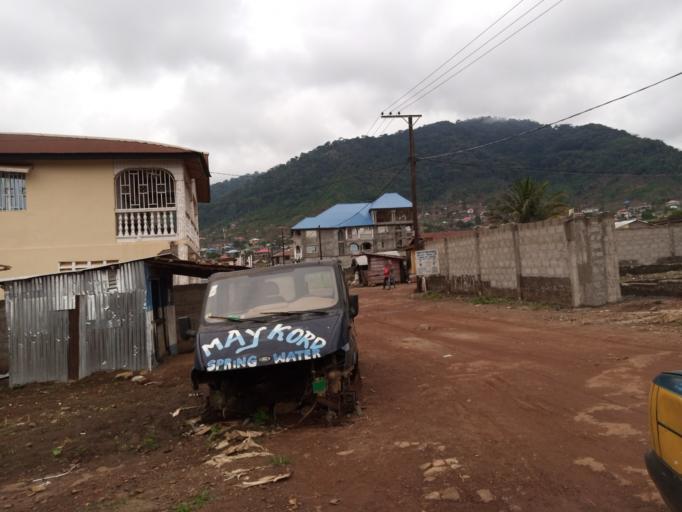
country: SL
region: Western Area
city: Hastings
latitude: 8.3786
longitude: -13.1515
